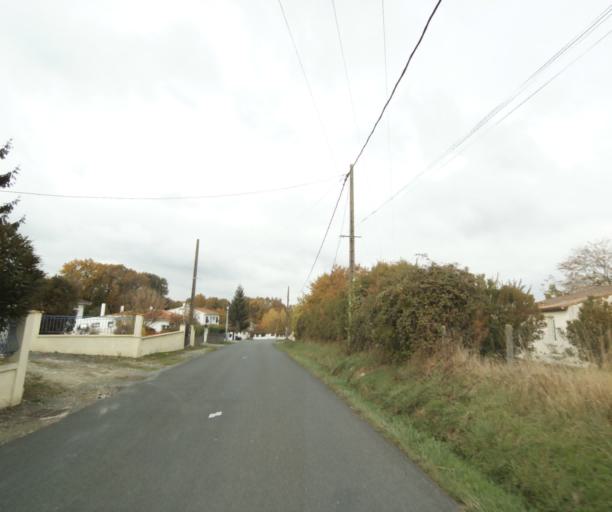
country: FR
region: Poitou-Charentes
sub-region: Departement de la Charente-Maritime
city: Bussac-sur-Charente
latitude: 45.7711
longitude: -0.6733
